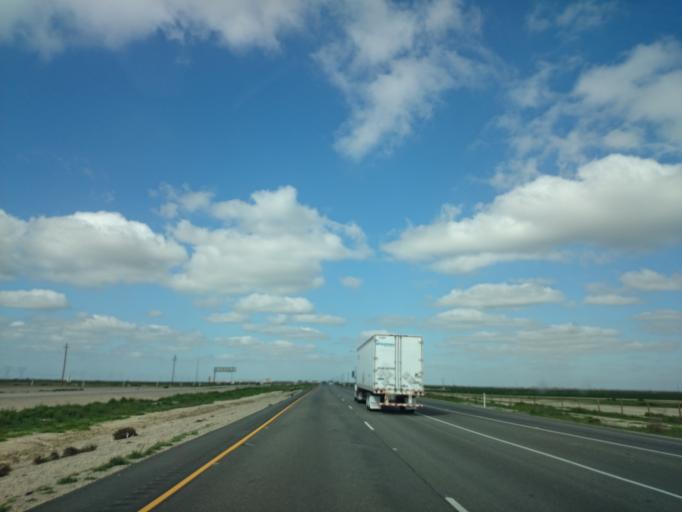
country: US
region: California
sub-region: Kern County
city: Rosedale
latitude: 35.2684
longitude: -119.2258
